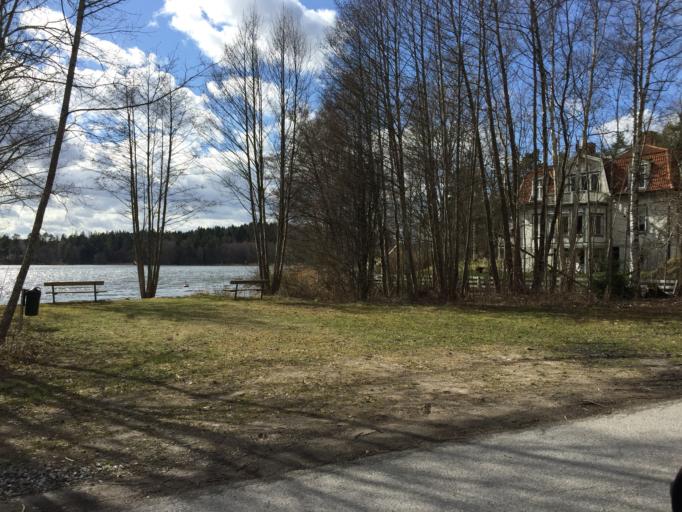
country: SE
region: Stockholm
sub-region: Botkyrka Kommun
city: Varsta
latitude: 59.1959
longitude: 17.8022
